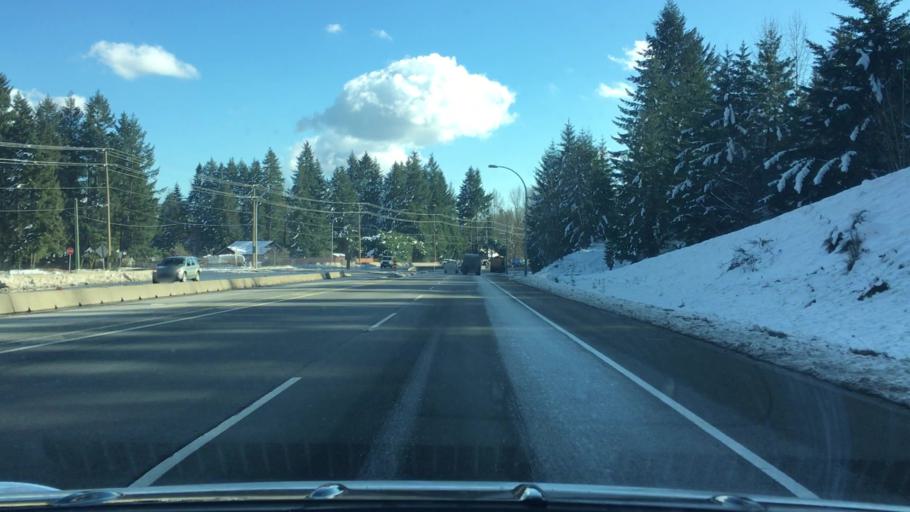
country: CA
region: British Columbia
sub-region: Cowichan Valley Regional District
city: Ladysmith
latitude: 49.0678
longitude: -123.8789
